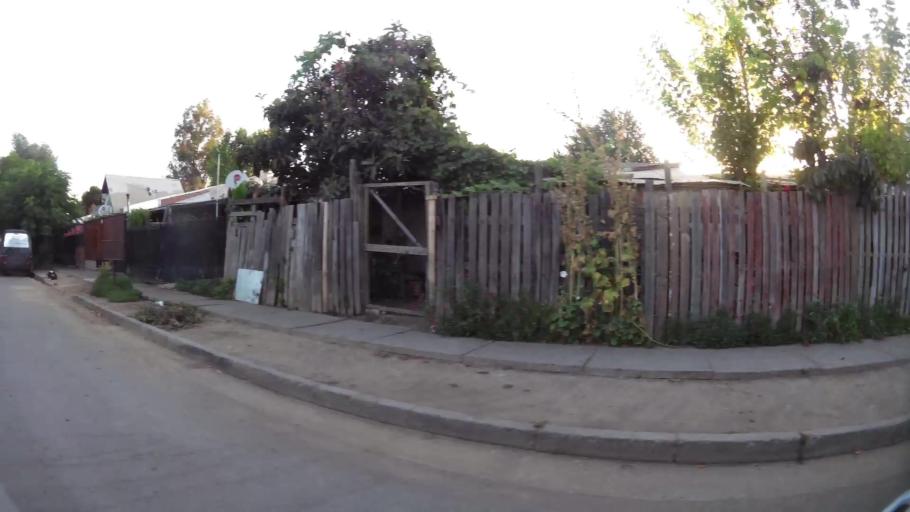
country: CL
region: Maule
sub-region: Provincia de Talca
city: Talca
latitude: -35.4477
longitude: -71.6367
